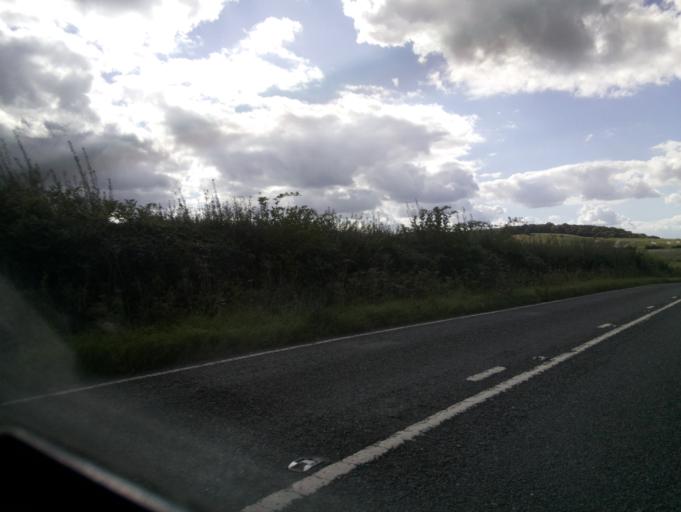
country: GB
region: England
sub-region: Hampshire
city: East Dean
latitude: 51.1138
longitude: -1.6090
